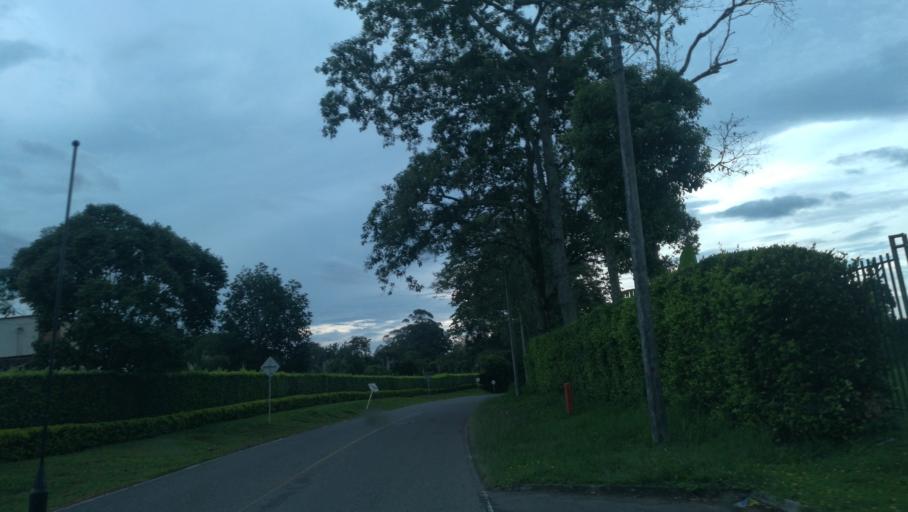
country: CO
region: Quindio
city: Montenegro
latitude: 4.5204
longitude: -75.7804
